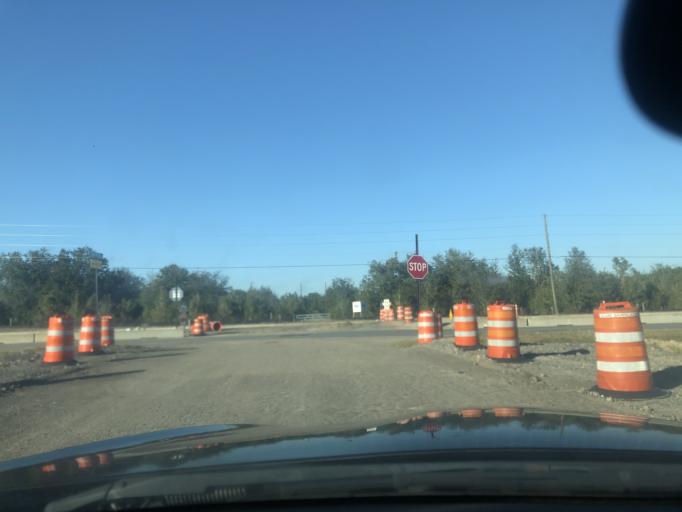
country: US
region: Florida
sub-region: Citrus County
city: Sugarmill Woods
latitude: 28.7637
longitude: -82.4944
